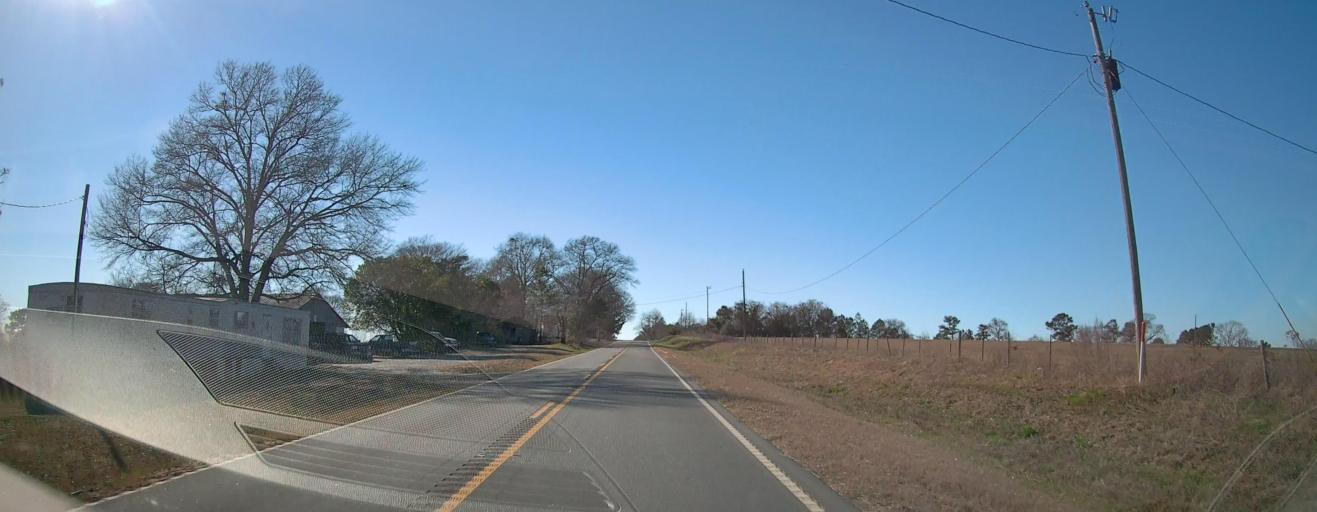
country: US
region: Georgia
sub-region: Taylor County
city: Butler
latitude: 32.6602
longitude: -84.3369
